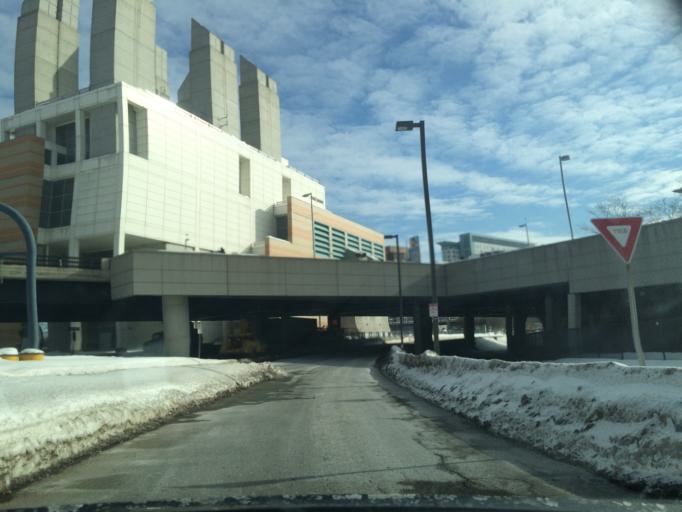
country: US
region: Massachusetts
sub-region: Suffolk County
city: South Boston
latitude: 42.3478
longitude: -71.0464
